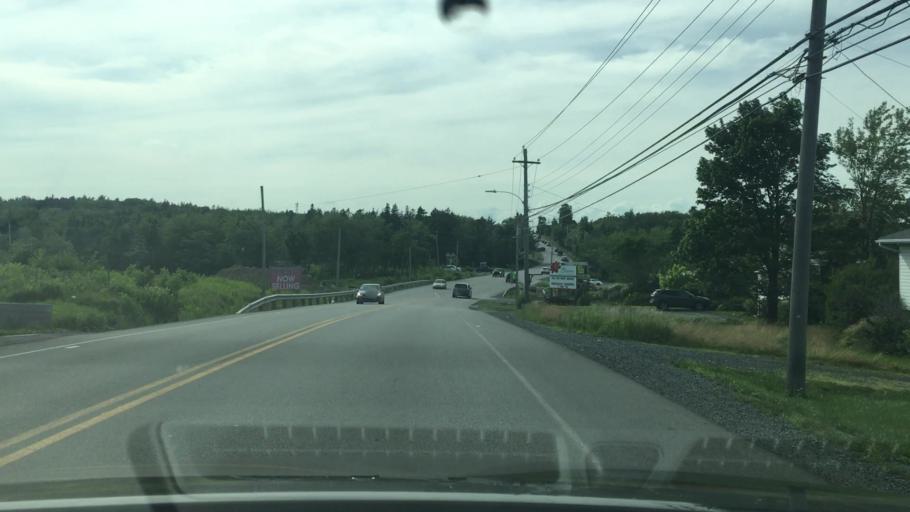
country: CA
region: Nova Scotia
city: Dartmouth
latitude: 44.7282
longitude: -63.7479
